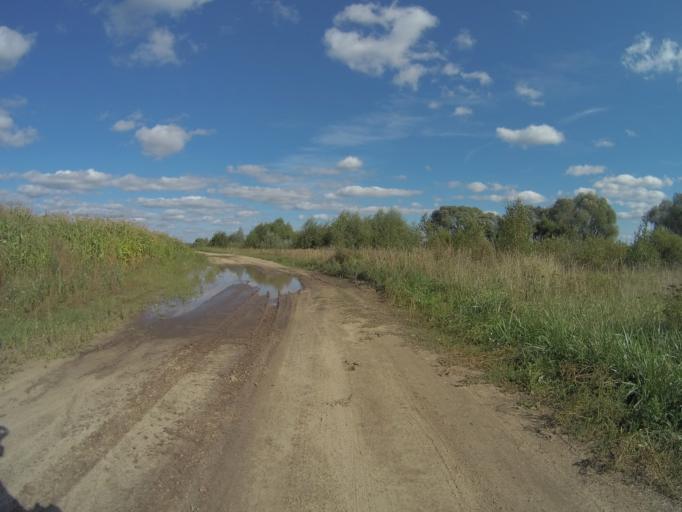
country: RU
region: Vladimir
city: Orgtrud
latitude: 56.3103
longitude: 40.6401
